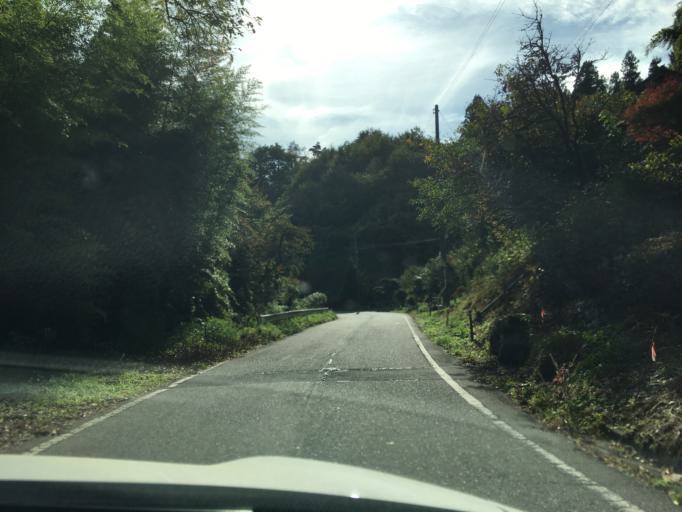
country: JP
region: Fukushima
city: Miharu
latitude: 37.5167
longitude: 140.5038
